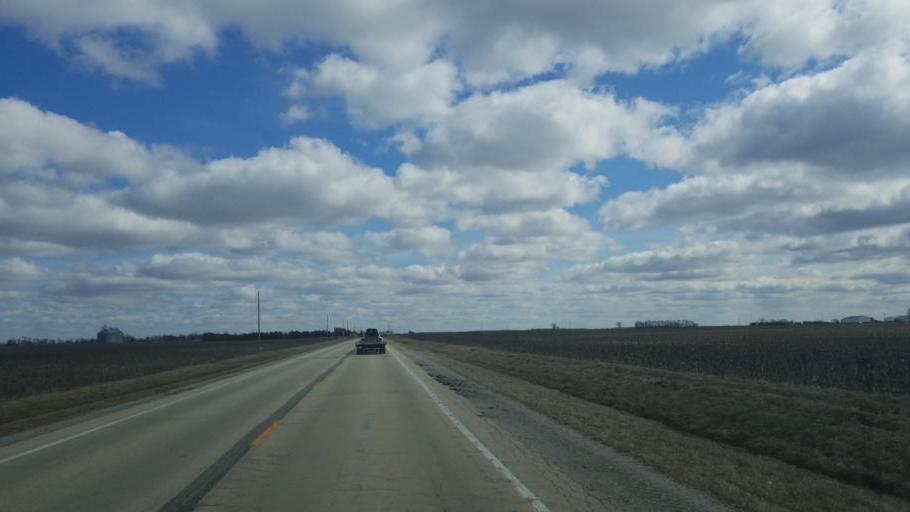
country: US
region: Illinois
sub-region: Douglas County
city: Atwood
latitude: 39.7920
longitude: -88.5558
